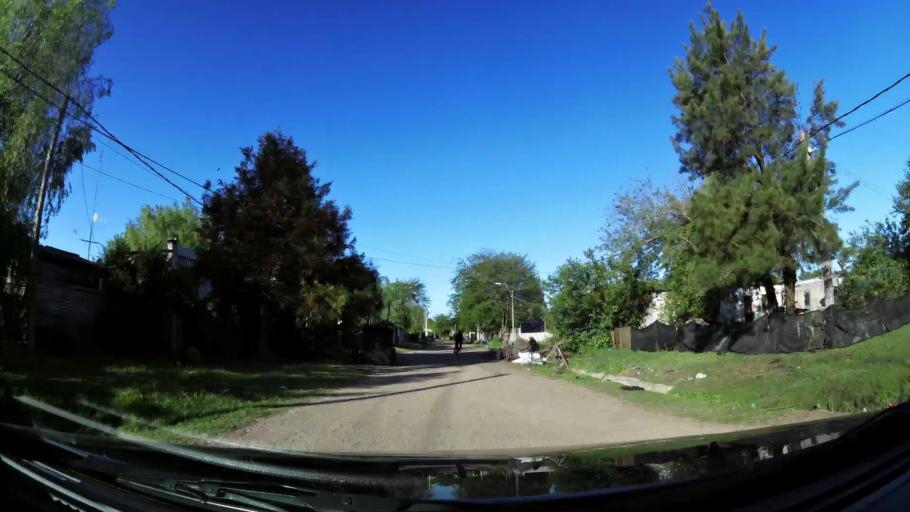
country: UY
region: Canelones
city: Paso de Carrasco
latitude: -34.8501
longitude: -56.0500
